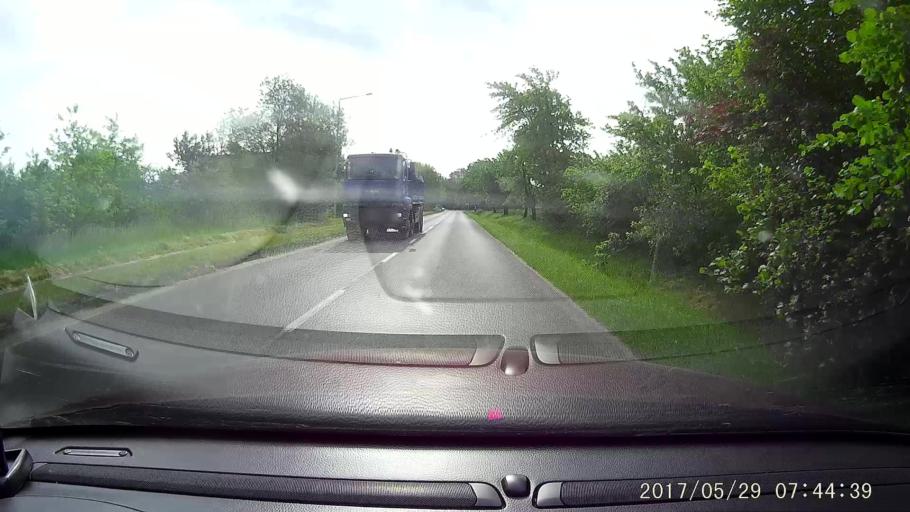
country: PL
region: Lower Silesian Voivodeship
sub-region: Powiat boleslawiecki
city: Boleslawiec
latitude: 51.2393
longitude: 15.6107
